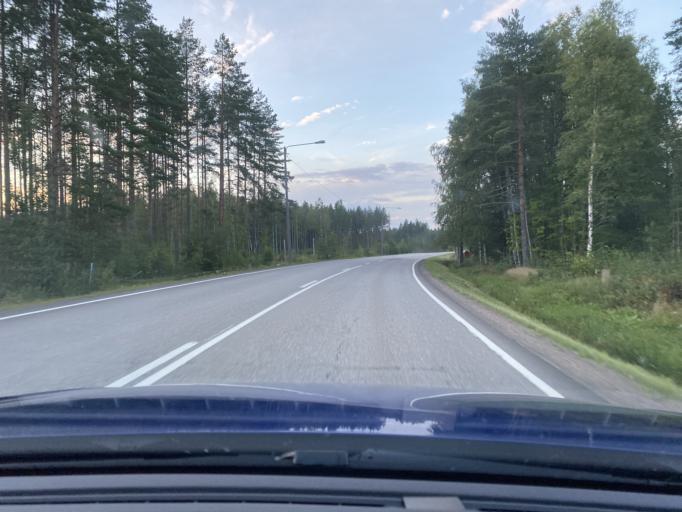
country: FI
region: Satakunta
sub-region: Pohjois-Satakunta
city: Honkajoki
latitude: 61.9706
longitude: 22.2219
